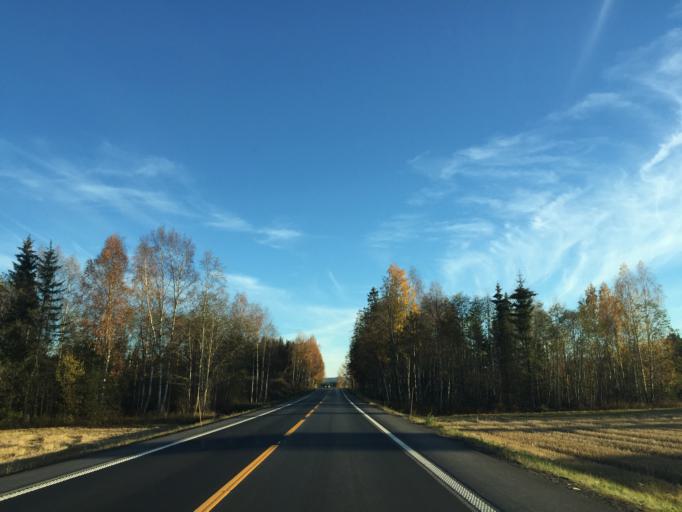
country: NO
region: Hedmark
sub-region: Kongsvinger
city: Spetalen
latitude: 60.2238
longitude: 11.8571
